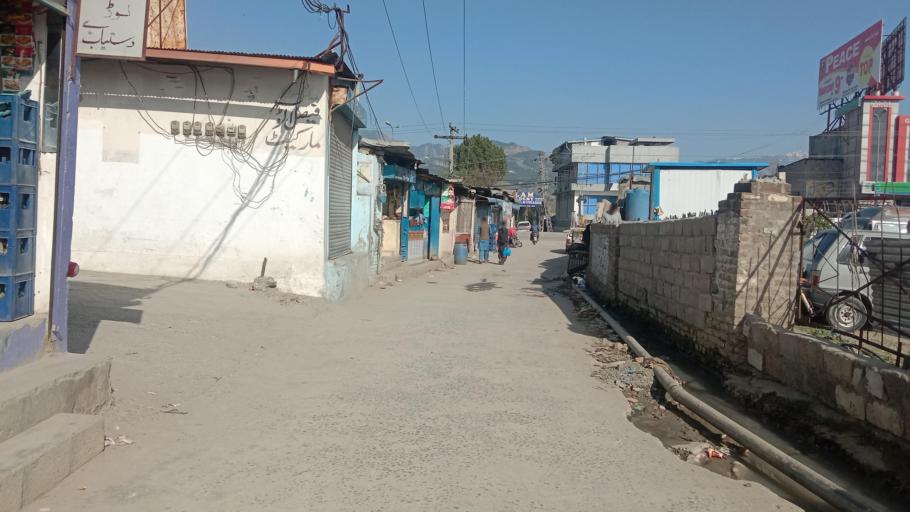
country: PK
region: Khyber Pakhtunkhwa
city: Abbottabad
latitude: 34.1782
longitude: 73.2280
